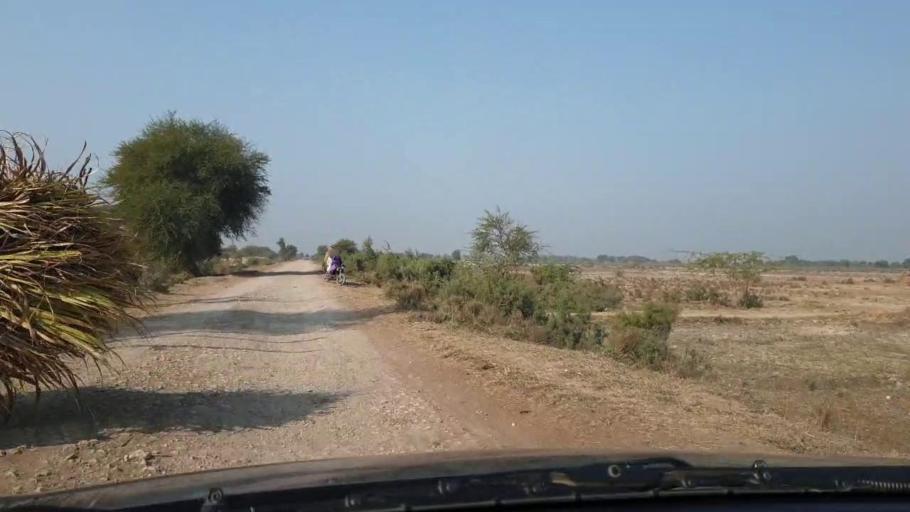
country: PK
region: Sindh
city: Jhol
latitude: 25.9616
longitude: 68.9591
